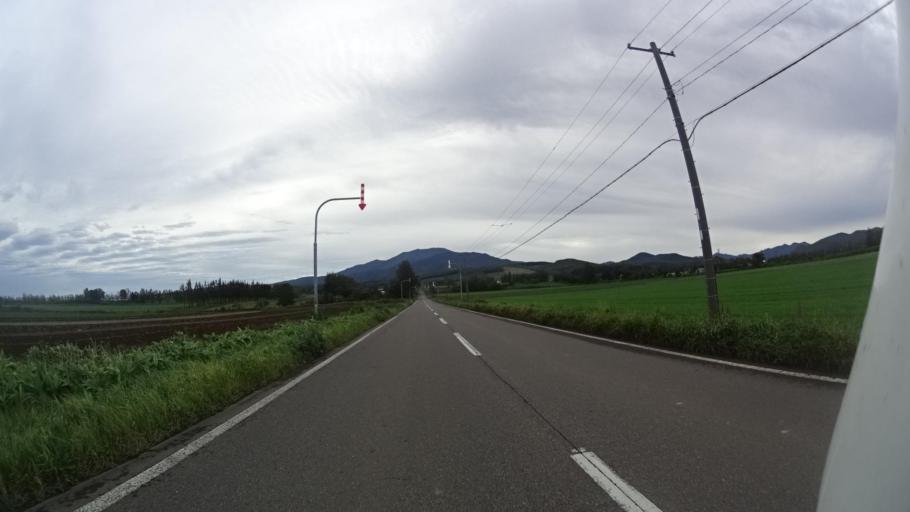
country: JP
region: Hokkaido
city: Shibetsu
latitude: 43.8741
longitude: 144.7403
